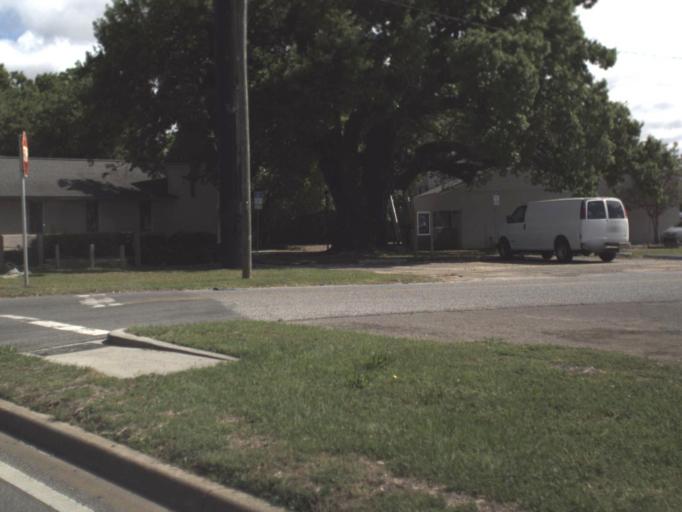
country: US
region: Florida
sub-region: Escambia County
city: West Pensacola
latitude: 30.4235
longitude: -87.2745
